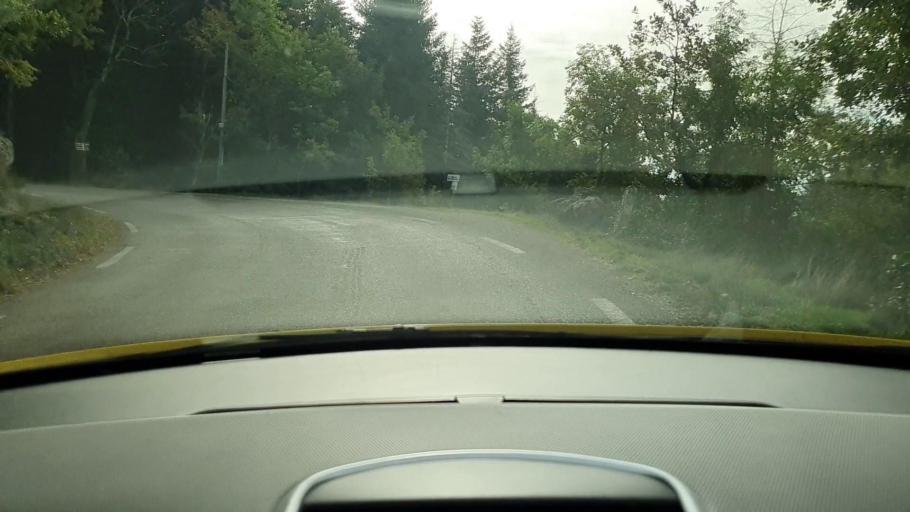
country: FR
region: Languedoc-Roussillon
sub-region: Departement du Gard
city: Le Vigan
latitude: 44.0248
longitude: 3.5708
